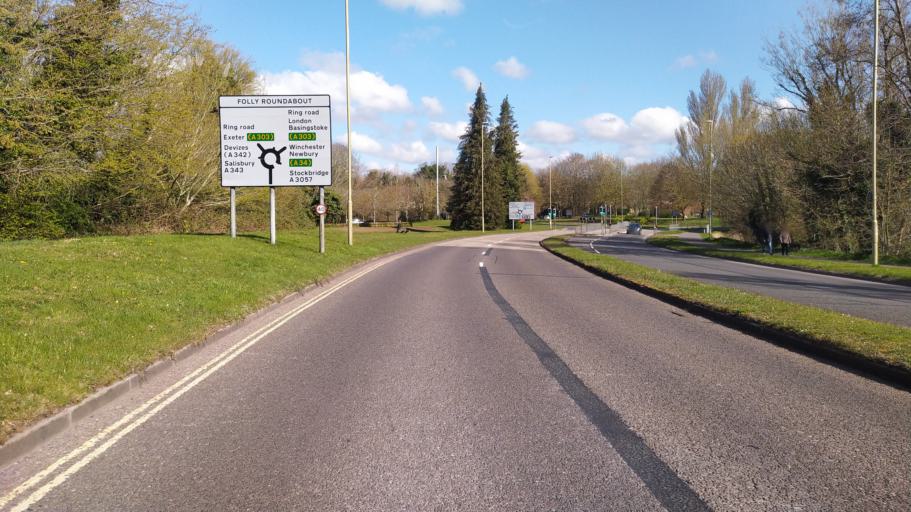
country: GB
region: England
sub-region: Hampshire
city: Andover
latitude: 51.2113
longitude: -1.4852
